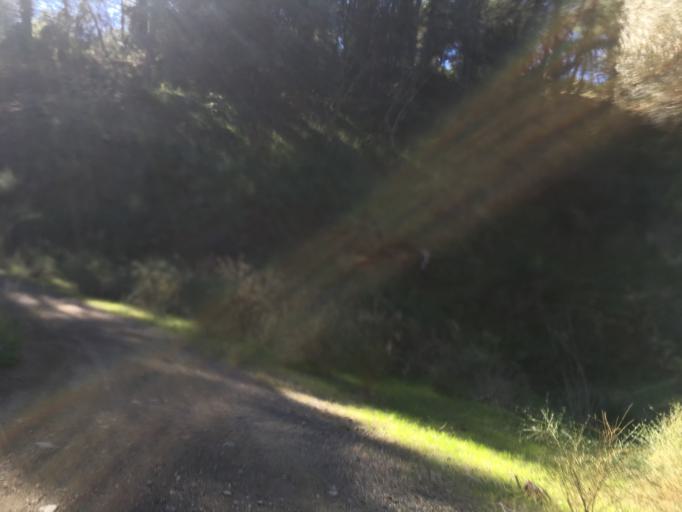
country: ES
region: Andalusia
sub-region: Provincia de Malaga
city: Malaga
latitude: 36.8030
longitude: -4.4056
